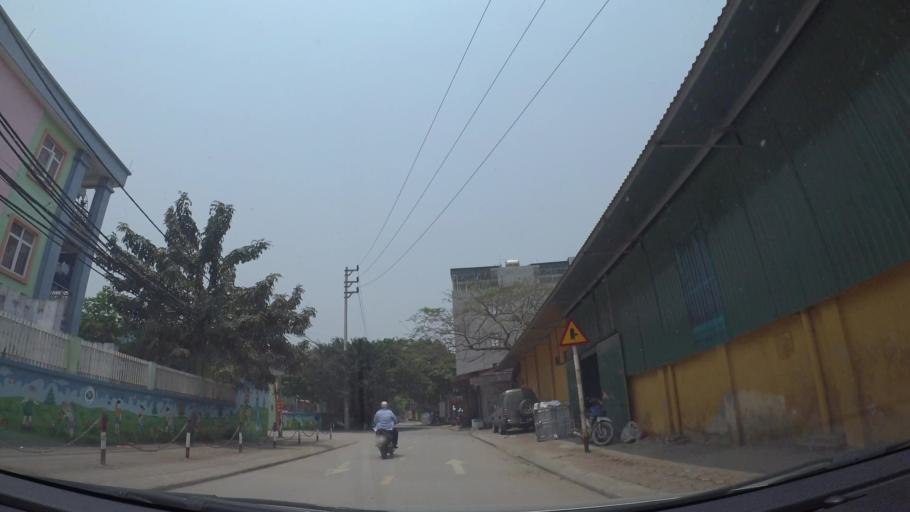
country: VN
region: Ha Noi
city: Ha Dong
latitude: 20.9936
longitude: 105.7745
